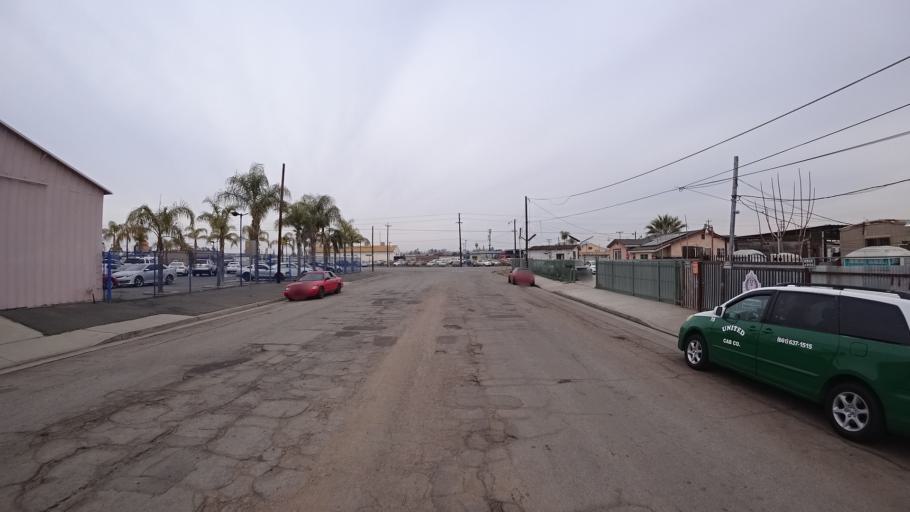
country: US
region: California
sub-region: Kern County
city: Bakersfield
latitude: 35.3725
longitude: -118.9810
